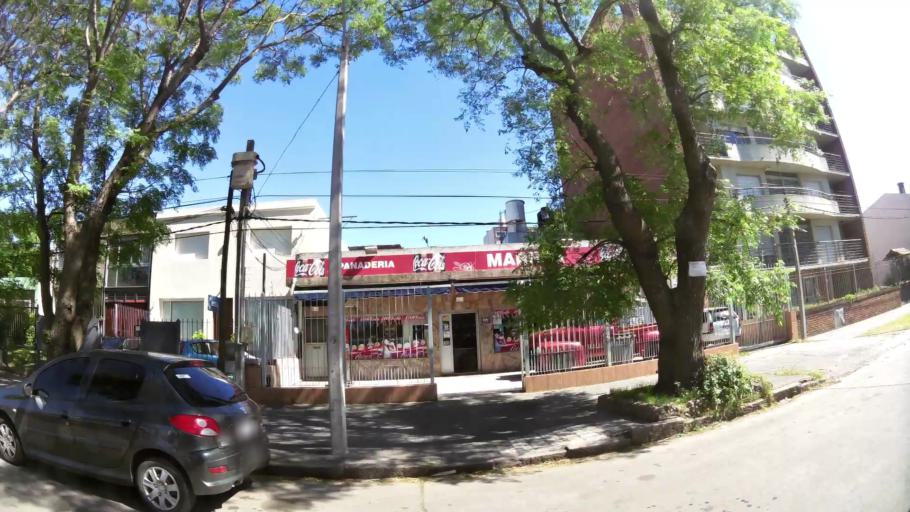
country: UY
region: Montevideo
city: Montevideo
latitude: -34.8909
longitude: -56.1190
